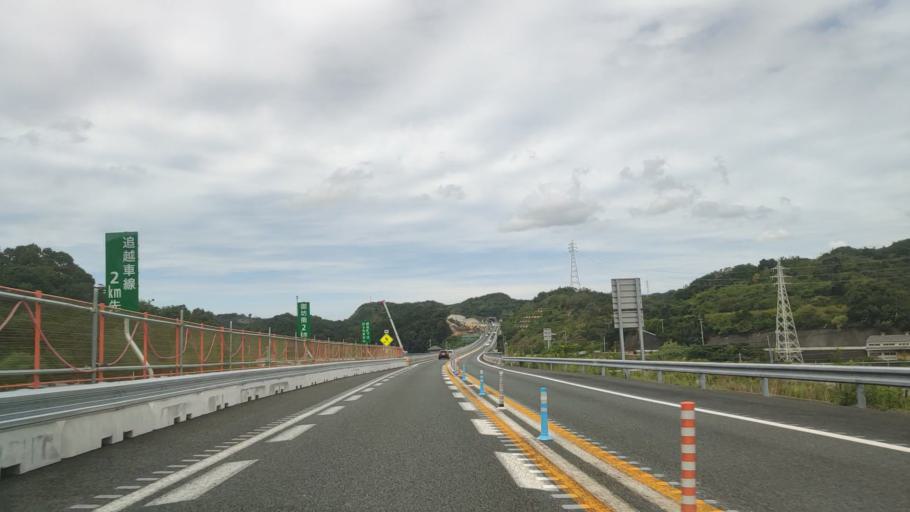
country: JP
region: Wakayama
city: Gobo
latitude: 33.8671
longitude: 135.1903
